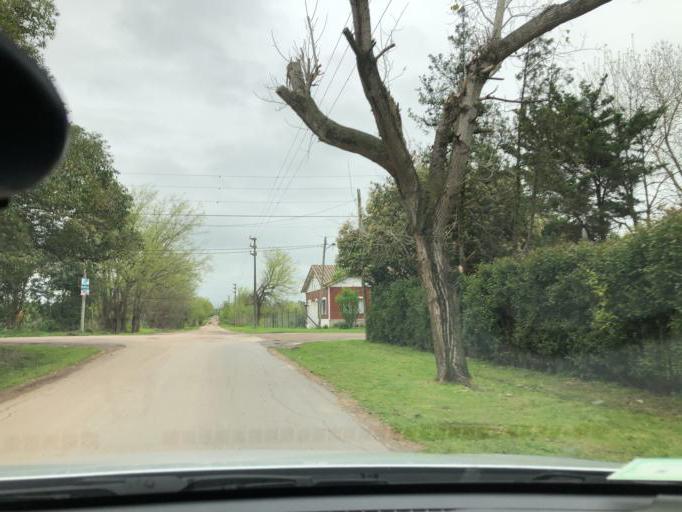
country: AR
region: Buenos Aires
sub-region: Partido de La Plata
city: La Plata
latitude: -34.9016
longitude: -58.0916
